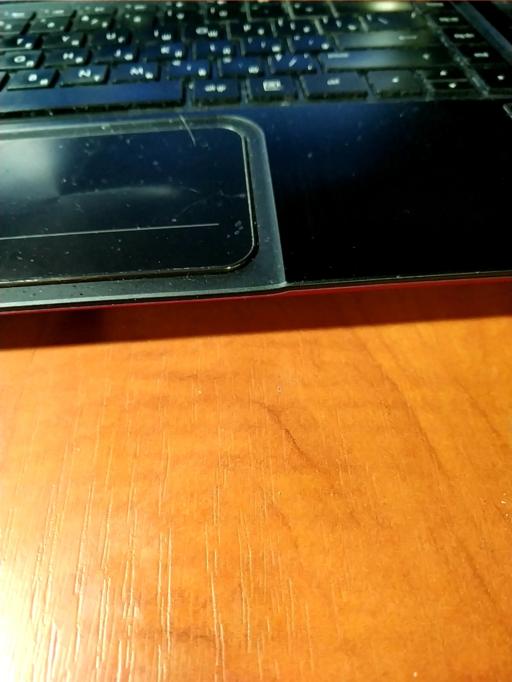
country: RU
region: Moskovskaya
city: Orekhovo-Zuyevo
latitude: 55.7673
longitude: 39.0062
